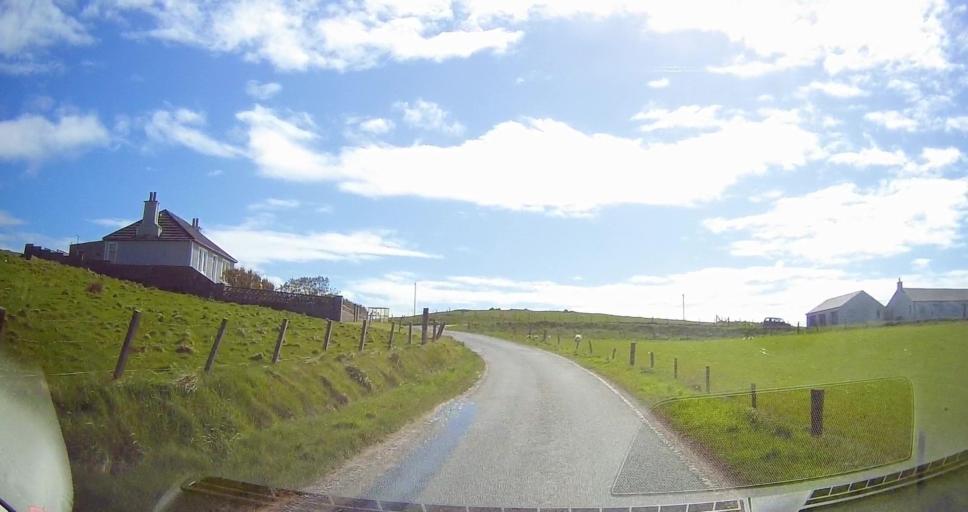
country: GB
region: Scotland
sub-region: Shetland Islands
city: Sandwick
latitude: 59.9401
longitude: -1.3230
